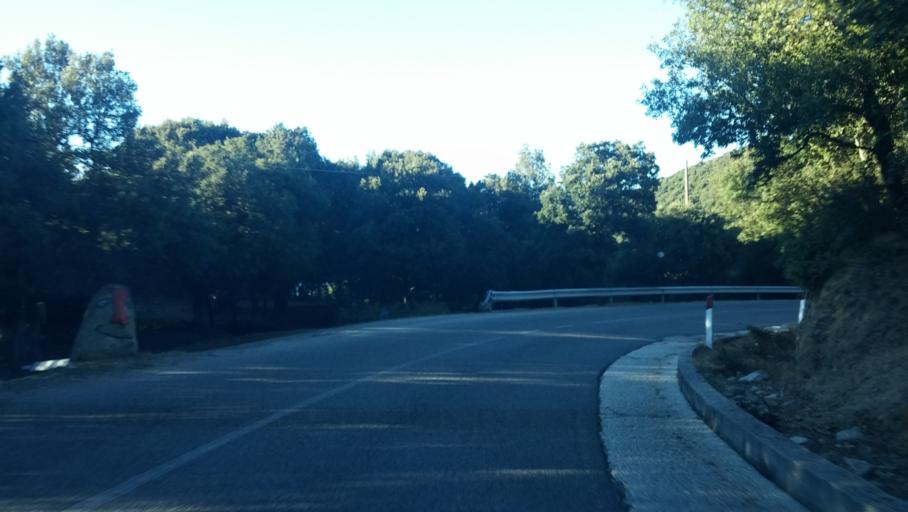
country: IT
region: Sardinia
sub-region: Provincia di Nuoro
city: Orgosolo
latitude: 40.1916
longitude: 9.3530
